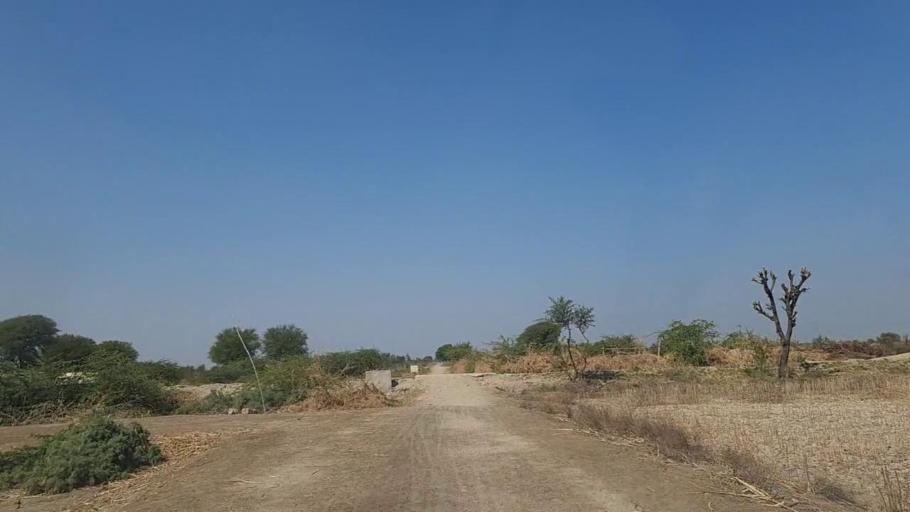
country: PK
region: Sindh
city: Digri
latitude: 25.2072
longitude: 69.1432
